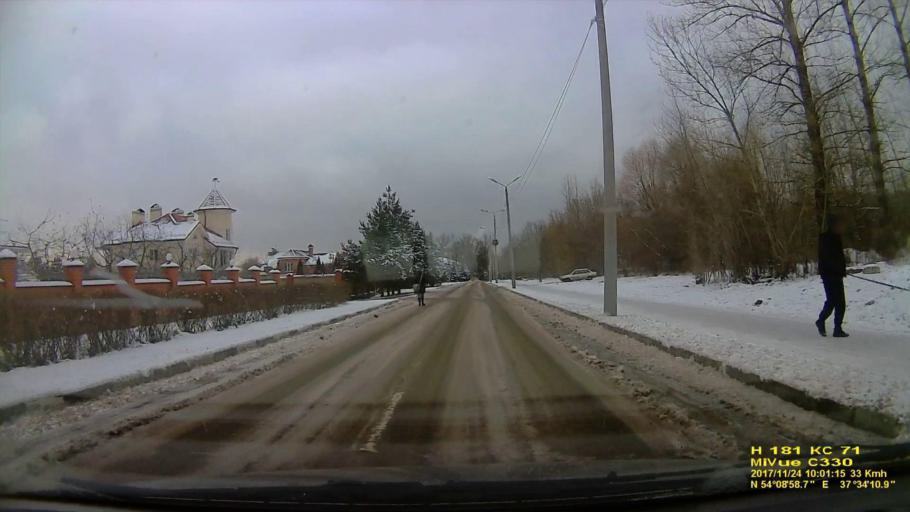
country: RU
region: Tula
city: Mendeleyevskiy
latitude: 54.1497
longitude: 37.5697
